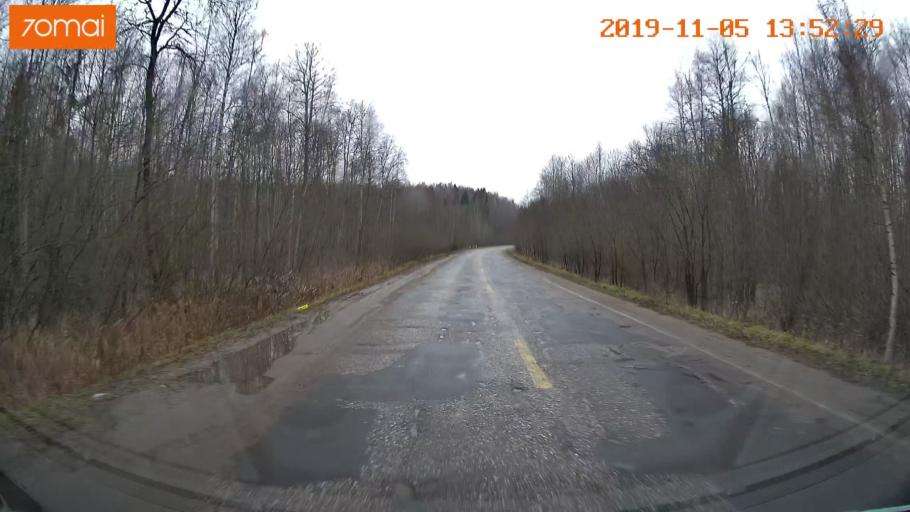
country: RU
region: Ivanovo
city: Kaminskiy
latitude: 57.0277
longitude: 41.3854
